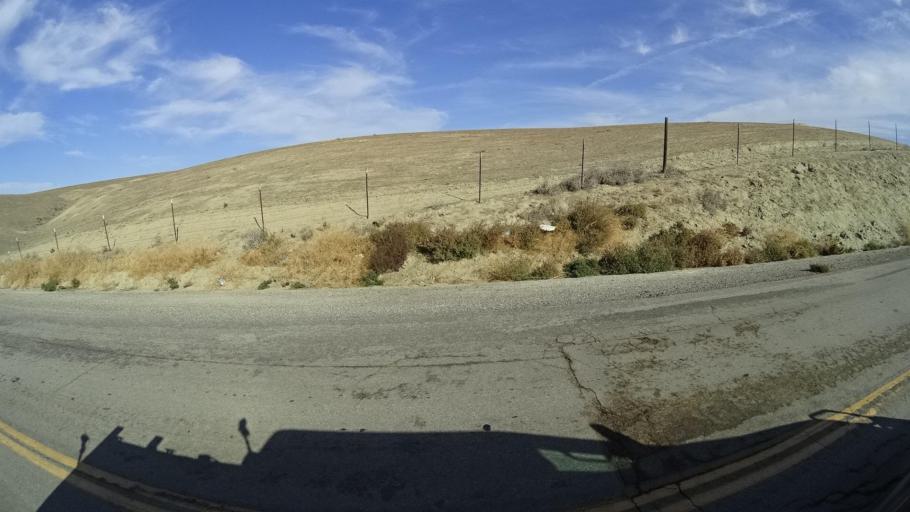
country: US
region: California
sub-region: Tulare County
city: Richgrove
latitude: 35.6219
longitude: -119.0151
